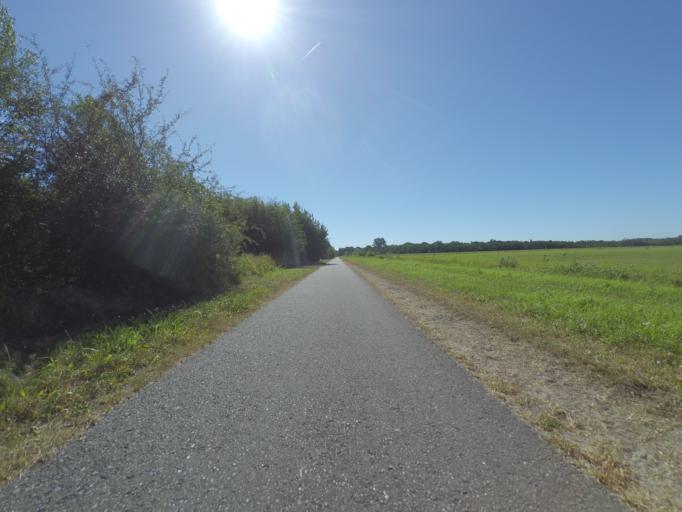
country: NL
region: Utrecht
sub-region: Gemeente Utrecht
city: Utrecht
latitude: 52.1344
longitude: 5.1225
